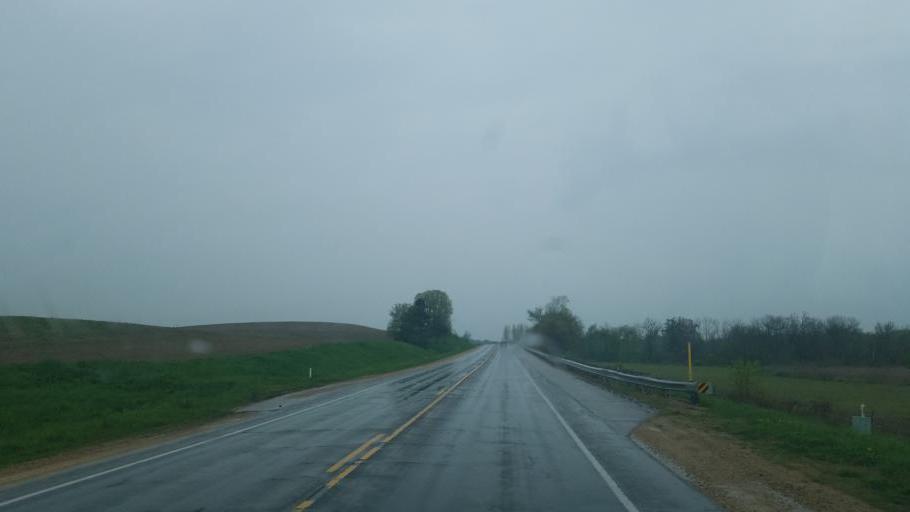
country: US
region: Wisconsin
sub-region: Sauk County
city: Reedsburg
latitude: 43.5491
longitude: -90.0567
